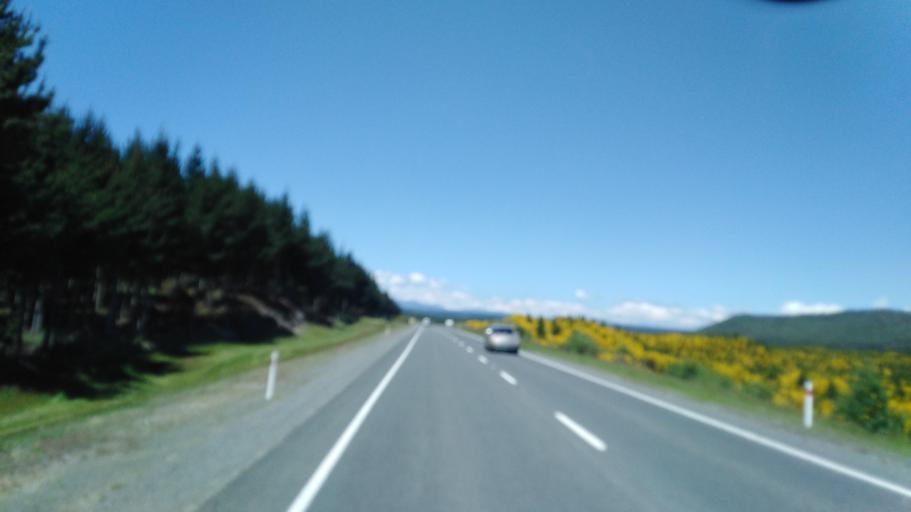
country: NZ
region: Waikato
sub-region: Taupo District
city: Taupo
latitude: -38.8314
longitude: 176.0658
